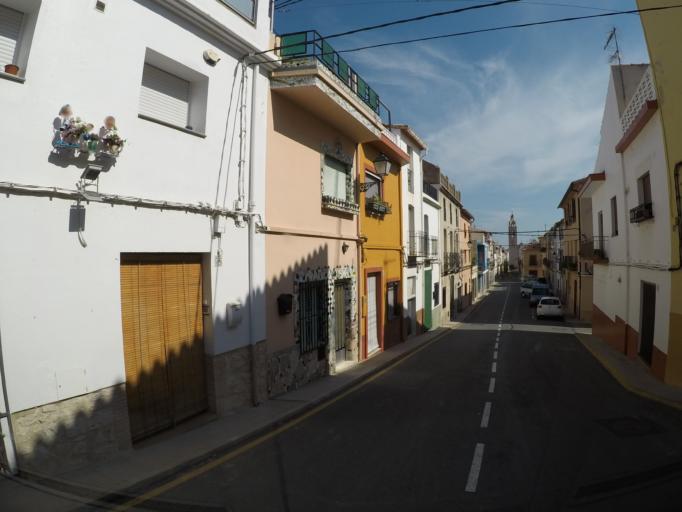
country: ES
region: Valencia
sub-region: Provincia de Alicante
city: Murla
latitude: 38.7791
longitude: -0.1042
